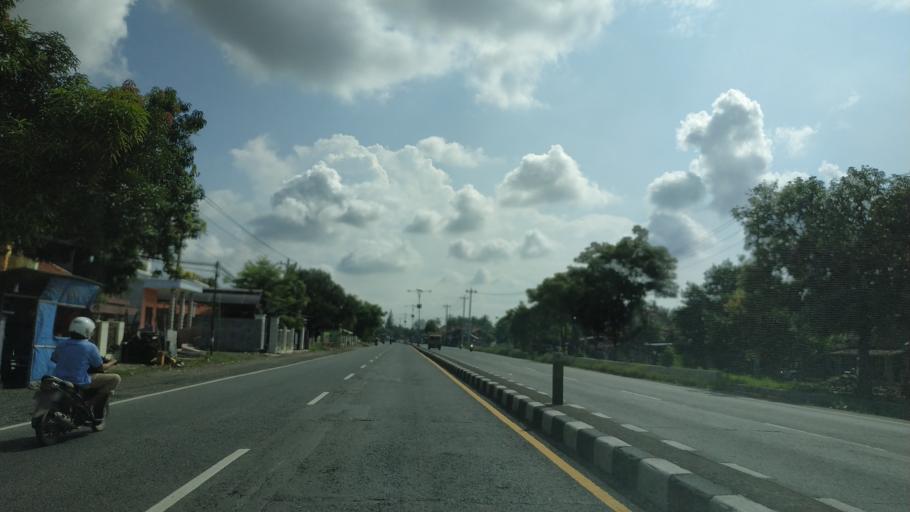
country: ID
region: Central Java
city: Comal
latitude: -6.8936
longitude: 109.5424
